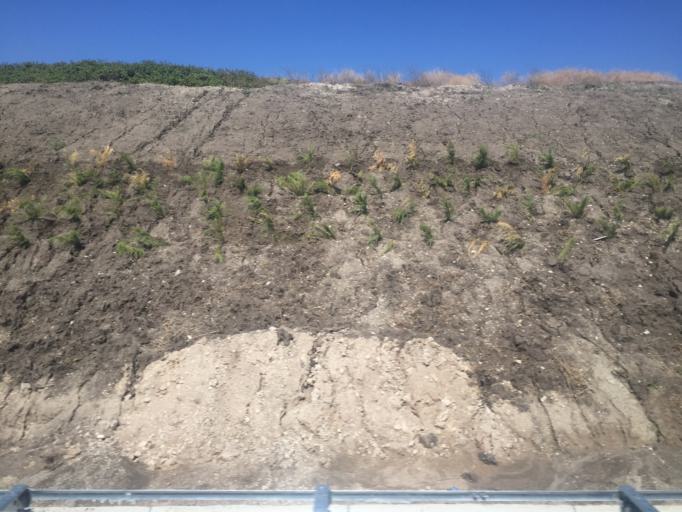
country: TR
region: Balikesir
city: Gobel
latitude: 40.0366
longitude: 28.2165
